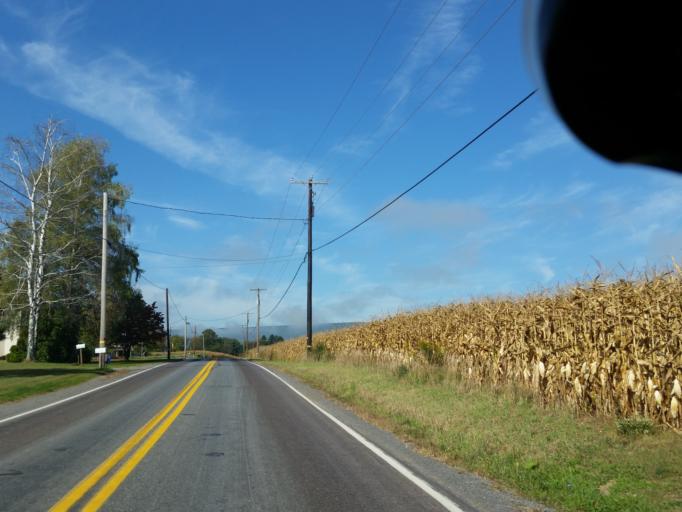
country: US
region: Pennsylvania
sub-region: Lycoming County
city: Duboistown
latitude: 41.1241
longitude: -76.9956
